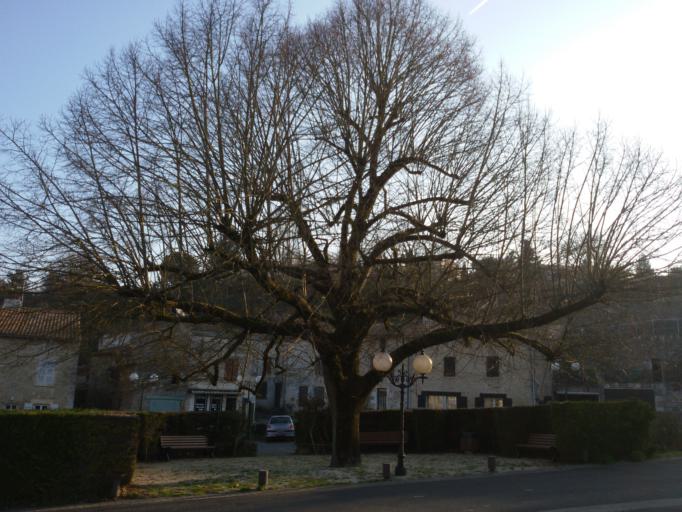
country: FR
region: Poitou-Charentes
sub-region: Departement des Deux-Sevres
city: Celles-sur-Belle
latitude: 46.2614
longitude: -0.2073
